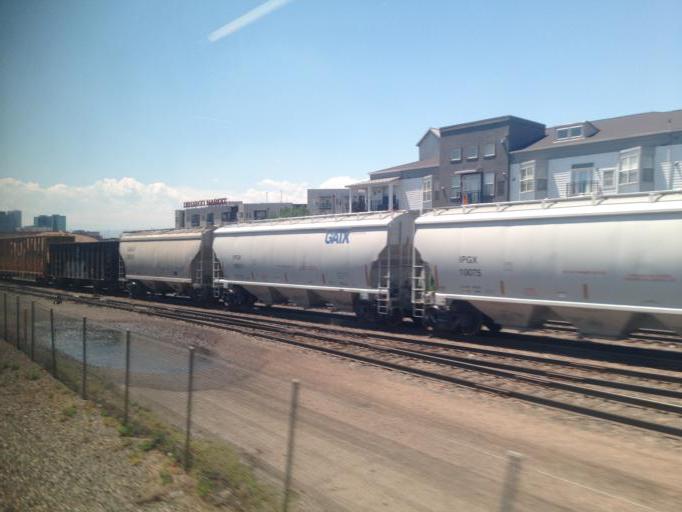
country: US
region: Colorado
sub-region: Denver County
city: Denver
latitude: 39.7622
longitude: -104.9865
